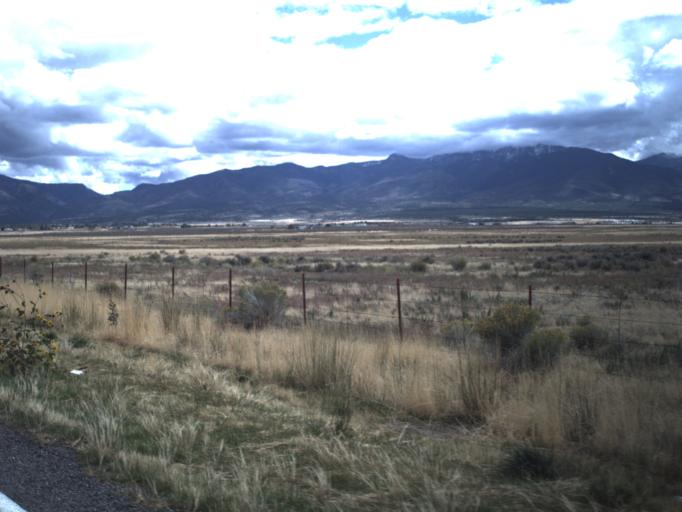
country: US
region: Utah
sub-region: Millard County
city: Fillmore
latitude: 38.9791
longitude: -112.3826
